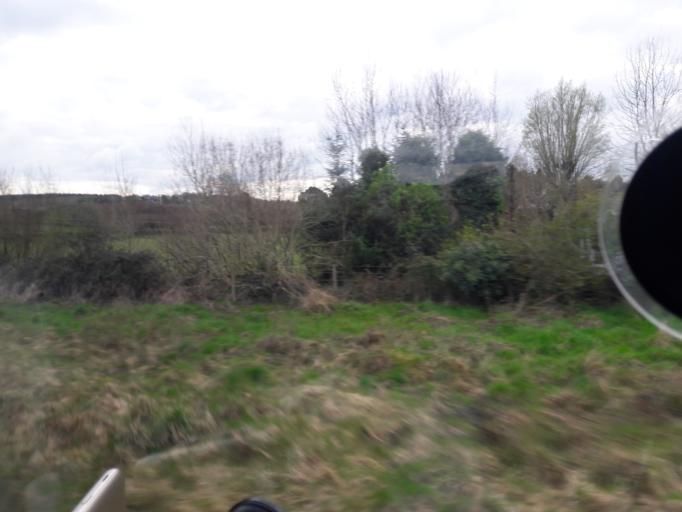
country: IE
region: Leinster
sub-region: An Iarmhi
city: Castlepollard
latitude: 53.6469
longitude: -7.4249
